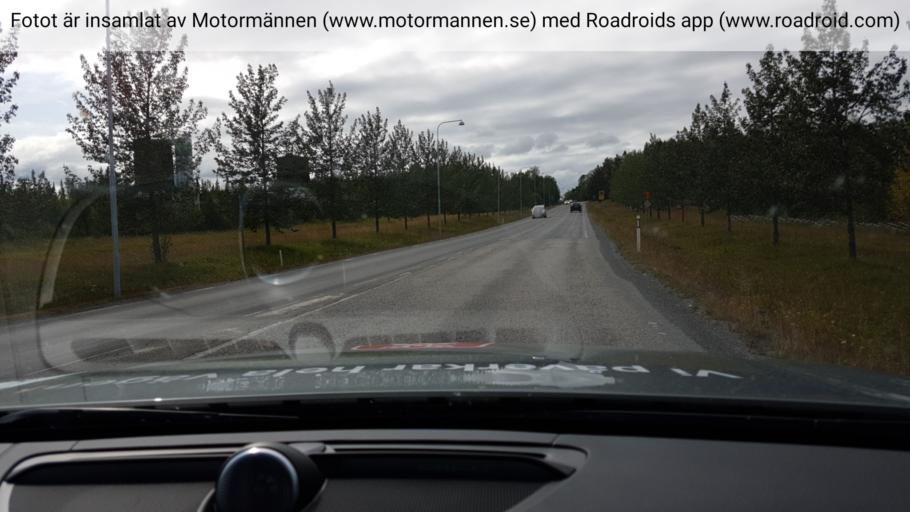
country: SE
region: Jaemtland
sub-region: OEstersunds Kommun
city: Ostersund
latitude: 63.1779
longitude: 14.6874
